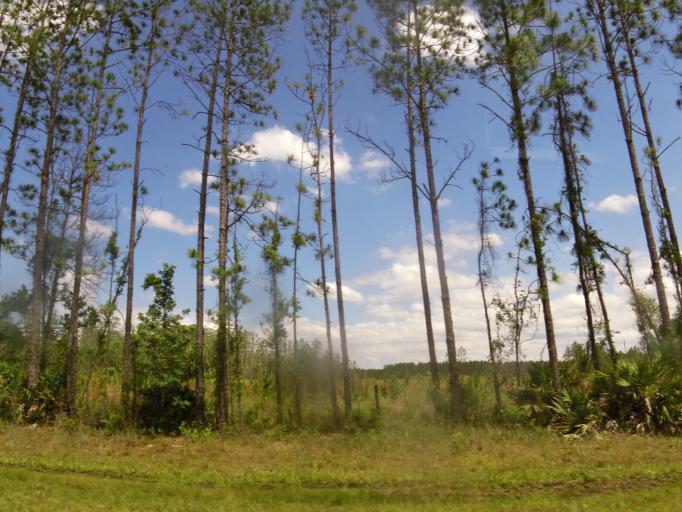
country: US
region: Florida
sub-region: Clay County
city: Green Cove Springs
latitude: 29.9304
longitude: -81.7535
